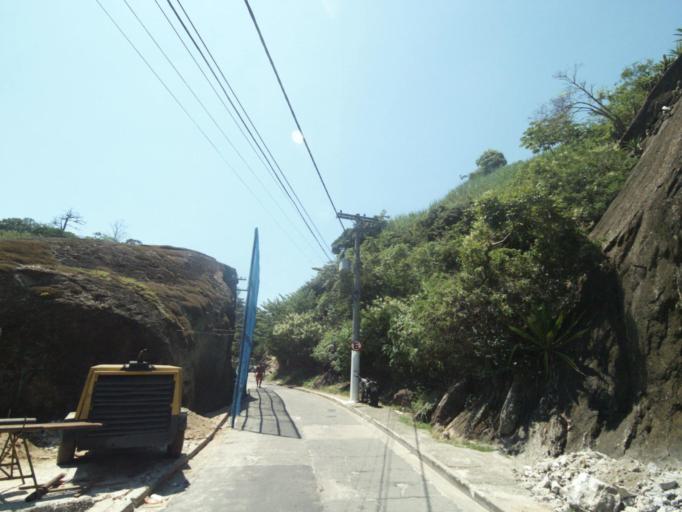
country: BR
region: Rio de Janeiro
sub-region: Niteroi
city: Niteroi
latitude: -22.9281
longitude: -43.1225
